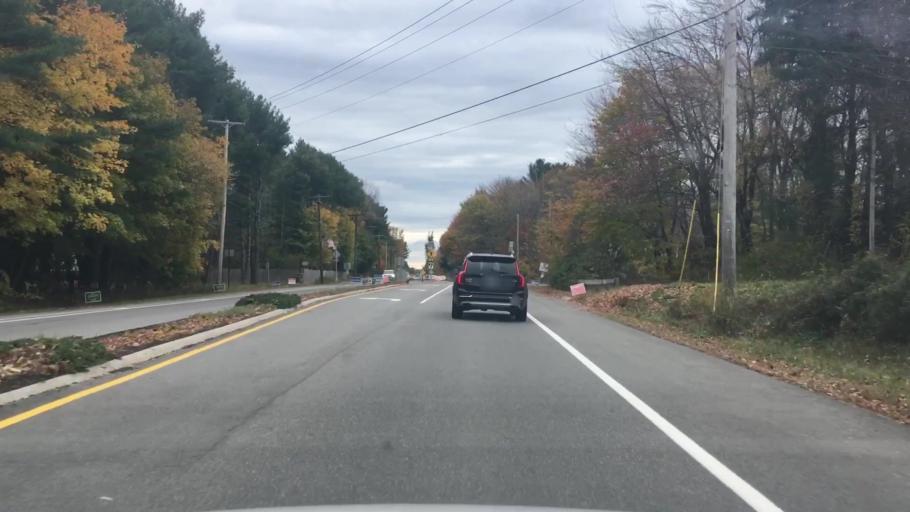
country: US
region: Maine
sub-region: Cumberland County
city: Falmouth
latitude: 43.7057
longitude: -70.2372
